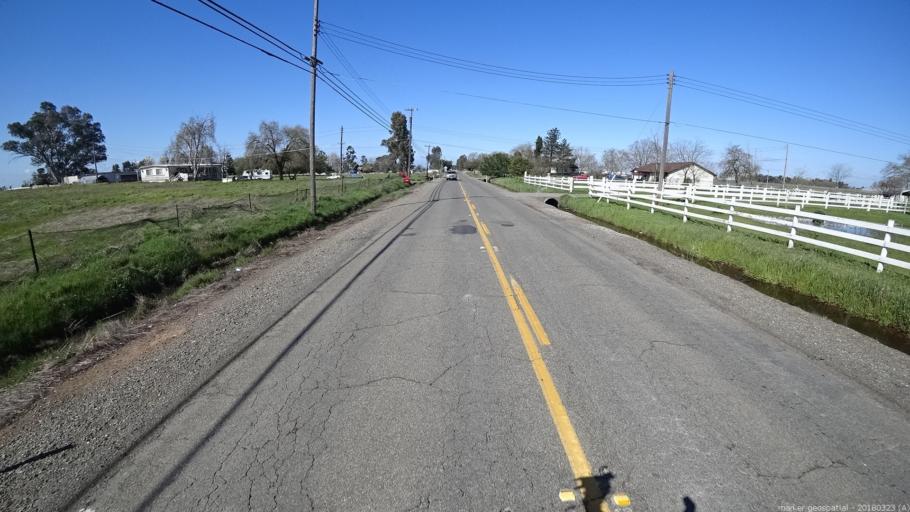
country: US
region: California
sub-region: Sacramento County
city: Elverta
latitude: 38.7326
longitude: -121.4754
